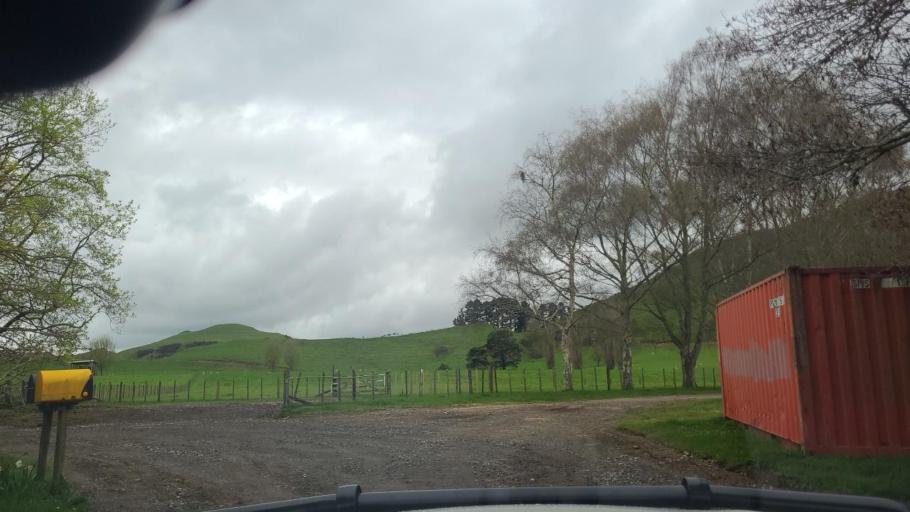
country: NZ
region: Taranaki
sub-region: South Taranaki District
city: Eltham
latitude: -39.3881
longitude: 174.4760
